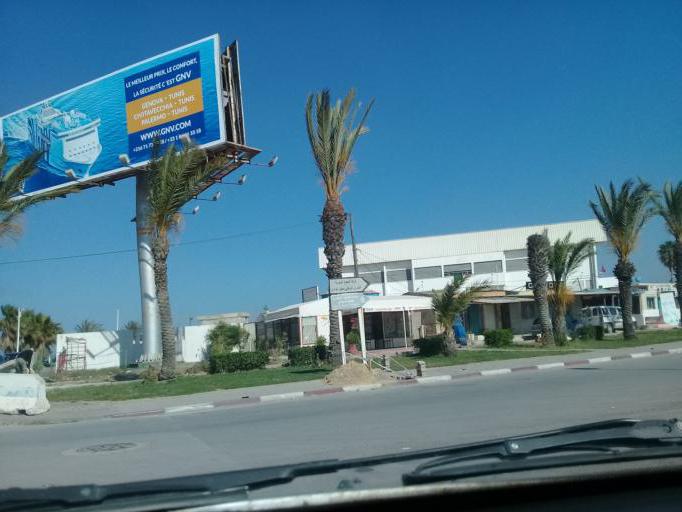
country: TN
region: Tunis
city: La Goulette
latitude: 36.8126
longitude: 10.3043
